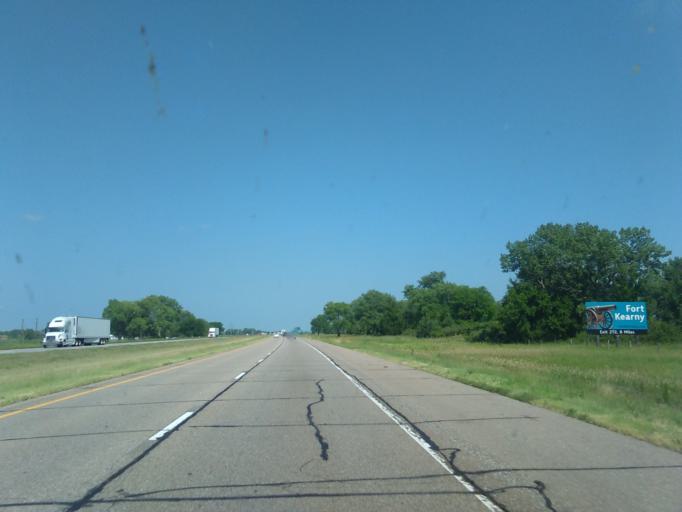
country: US
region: Nebraska
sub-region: Buffalo County
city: Kearney
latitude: 40.6700
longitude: -99.1458
